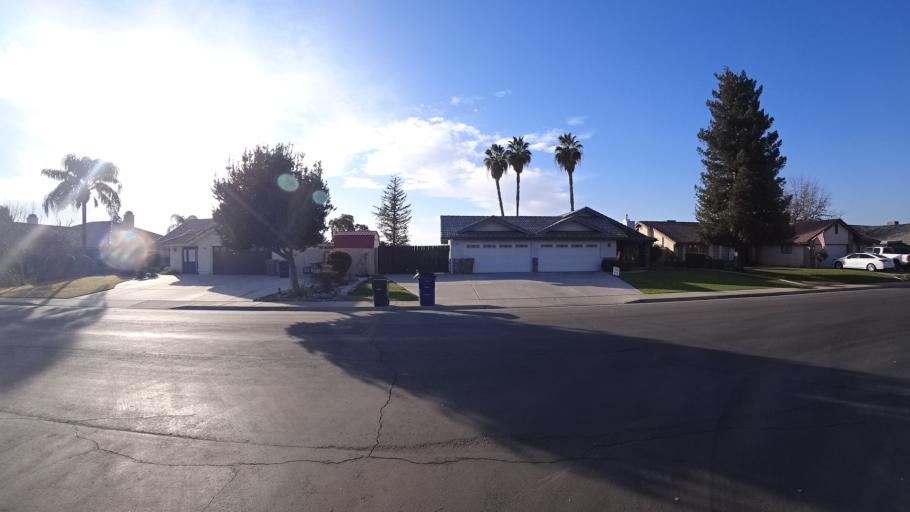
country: US
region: California
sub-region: Kern County
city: Rosedale
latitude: 35.3477
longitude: -119.1561
